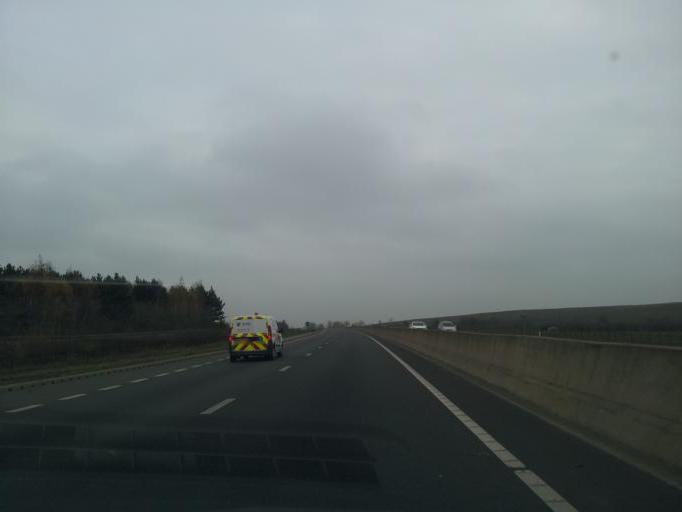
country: GB
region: England
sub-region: Bedford
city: Wootton
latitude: 52.0802
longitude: -0.5297
